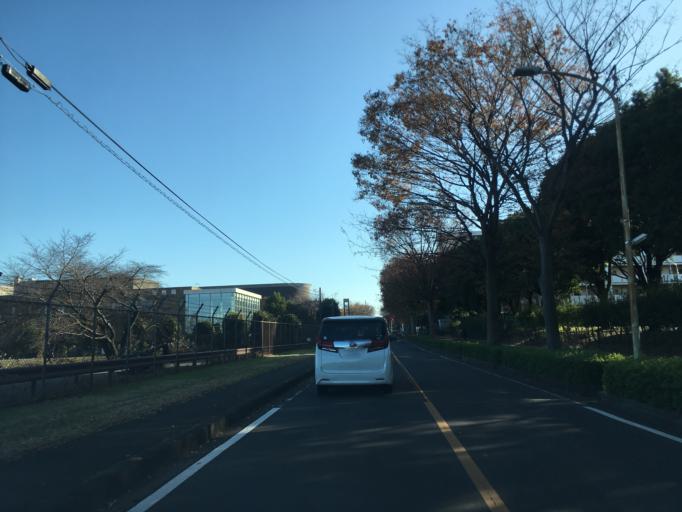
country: JP
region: Saitama
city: Tokorozawa
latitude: 35.8029
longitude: 139.4715
